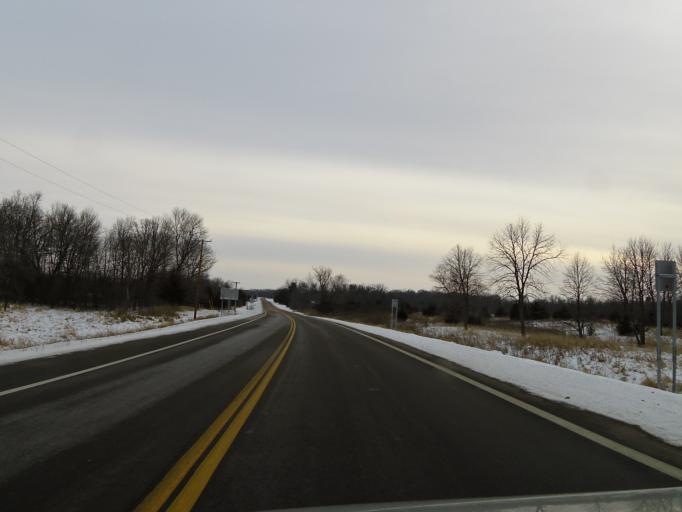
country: US
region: Minnesota
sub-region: Hennepin County
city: Saint Bonifacius
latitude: 44.8890
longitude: -93.7053
